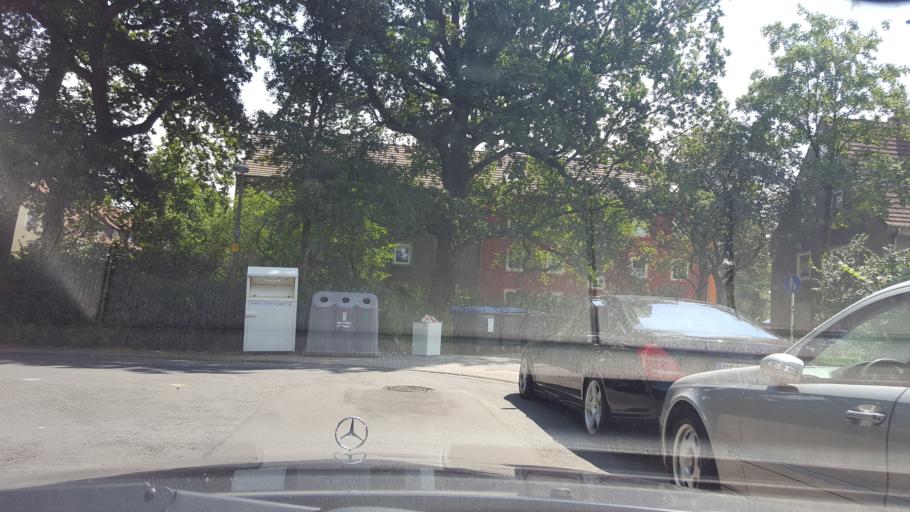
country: DE
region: North Rhine-Westphalia
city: Marl
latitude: 51.6664
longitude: 7.1205
